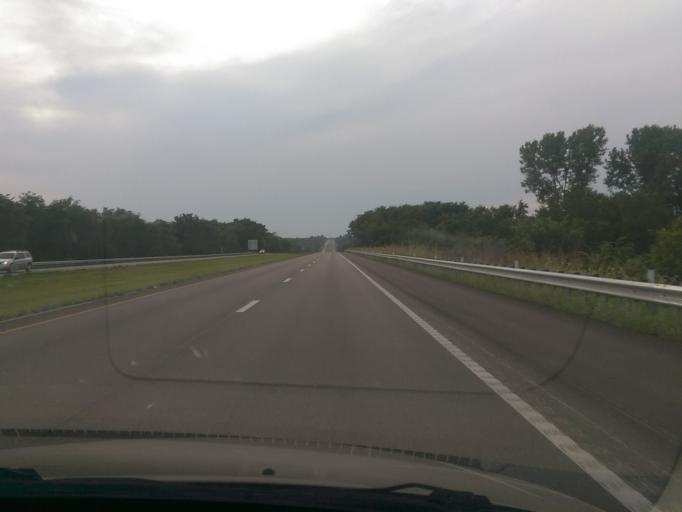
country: US
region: Missouri
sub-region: Andrew County
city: Savannah
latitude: 39.8956
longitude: -94.8713
